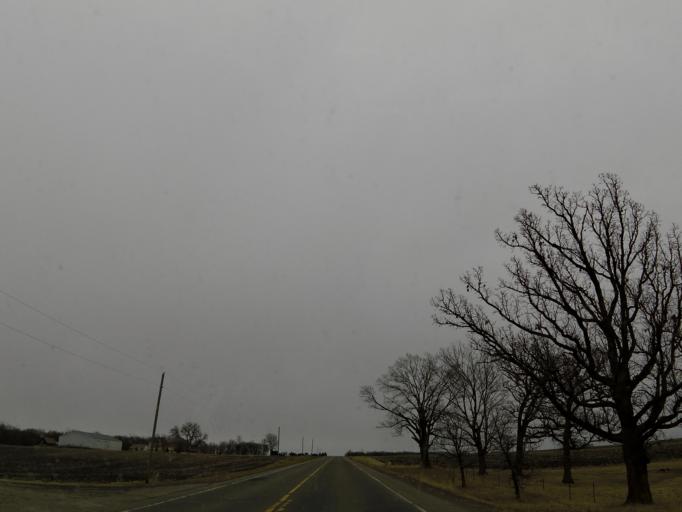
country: US
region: Minnesota
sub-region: Le Sueur County
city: Le Sueur
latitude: 44.5431
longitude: -93.8768
